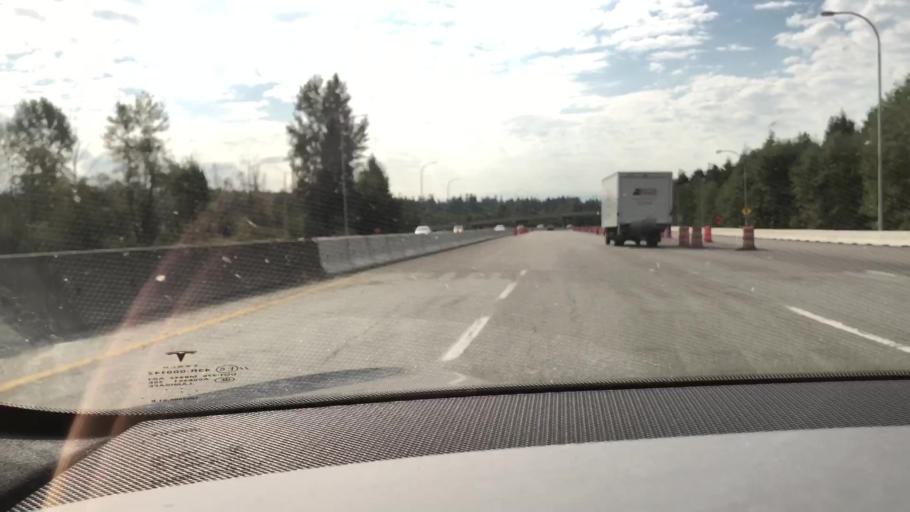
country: CA
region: British Columbia
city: Delta
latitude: 49.1366
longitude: -122.9311
